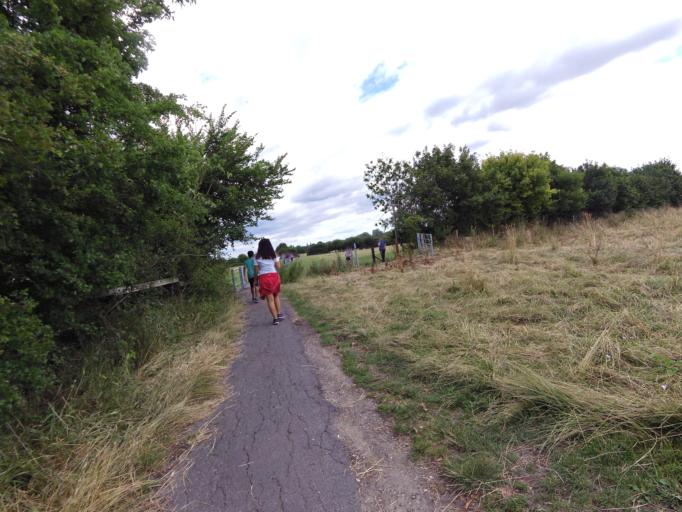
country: GB
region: England
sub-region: Cambridgeshire
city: Grantchester
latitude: 52.1814
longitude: 0.0971
